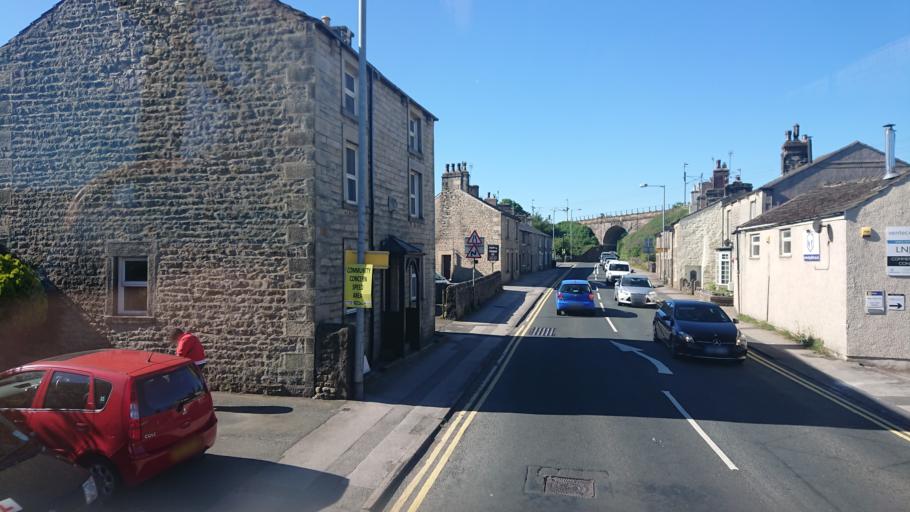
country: GB
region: England
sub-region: Lancashire
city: Galgate
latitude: 53.9915
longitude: -2.7891
